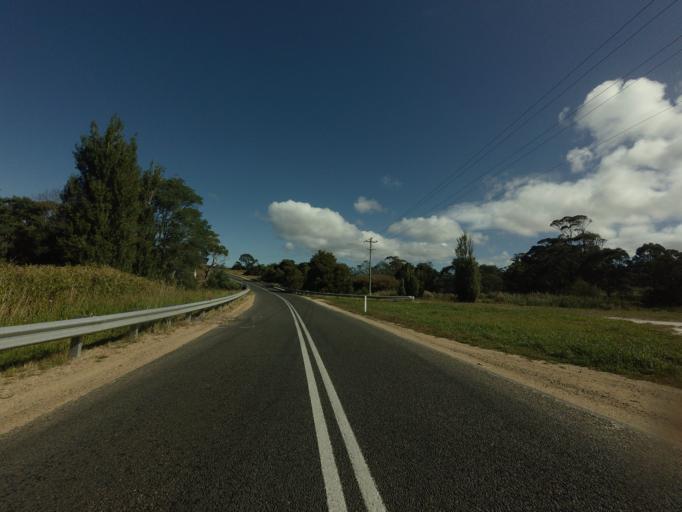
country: AU
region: Tasmania
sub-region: Break O'Day
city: St Helens
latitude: -41.7420
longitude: 148.2730
